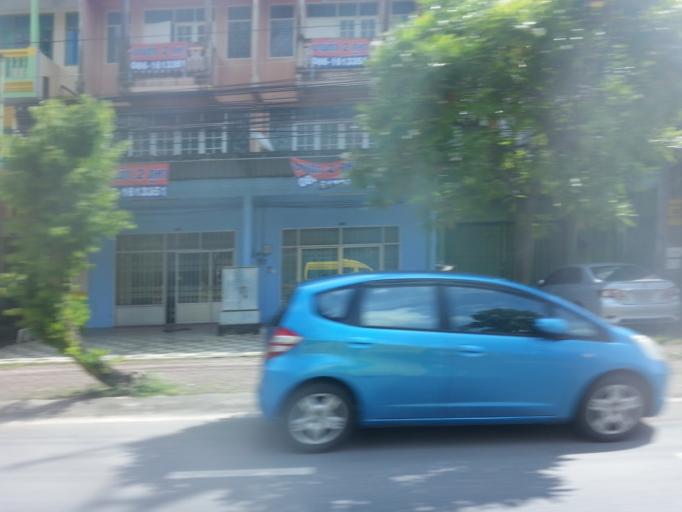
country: TH
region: Phuket
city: Kathu
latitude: 7.9085
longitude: 98.3312
